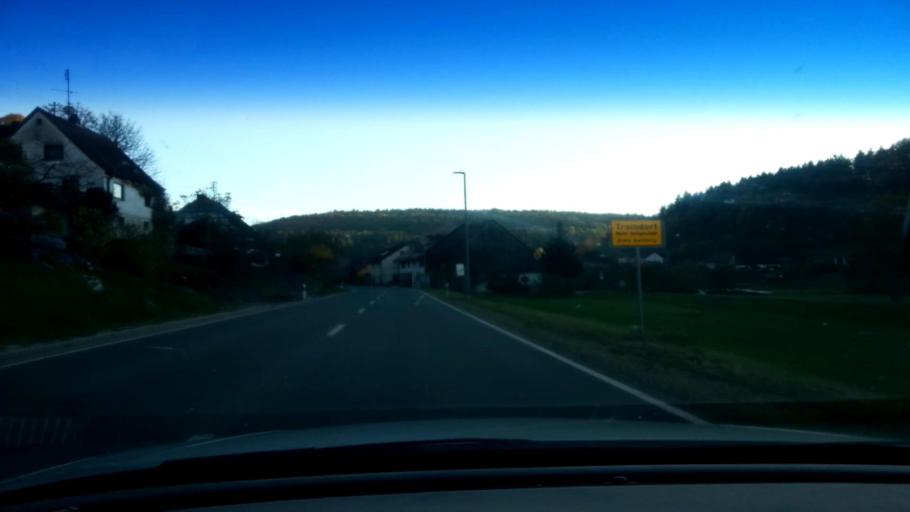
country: DE
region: Bavaria
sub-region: Upper Franconia
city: Heiligenstadt
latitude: 49.8597
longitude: 11.1774
